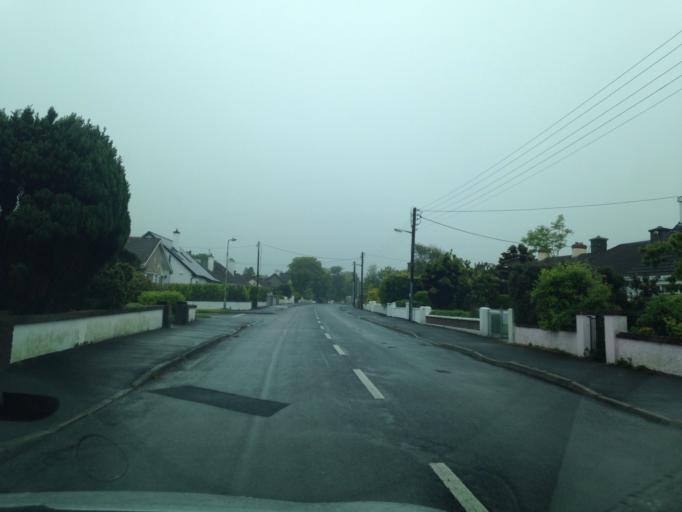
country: IE
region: Connaught
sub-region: County Galway
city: Gaillimh
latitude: 53.2742
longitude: -9.0279
